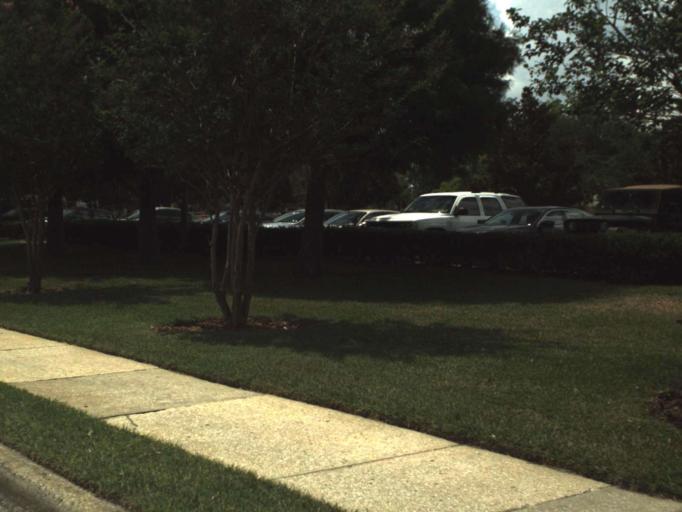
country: US
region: Florida
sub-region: Lake County
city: Leesburg
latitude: 28.8067
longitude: -81.8687
